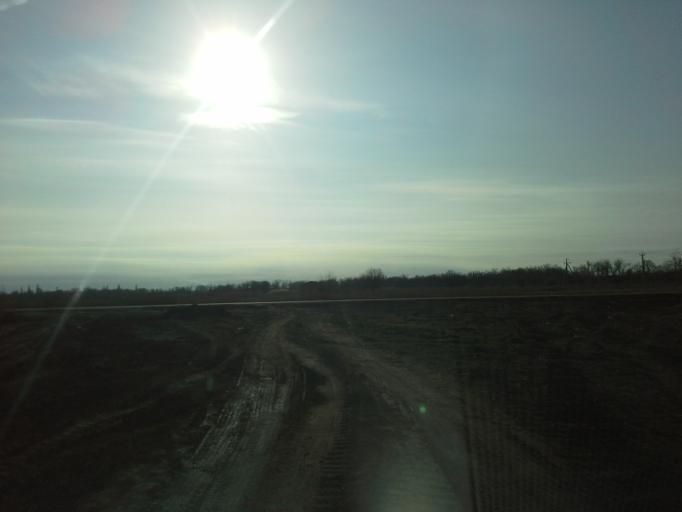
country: RU
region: Volgograd
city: Krasnoslobodsk
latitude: 48.6751
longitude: 44.5537
